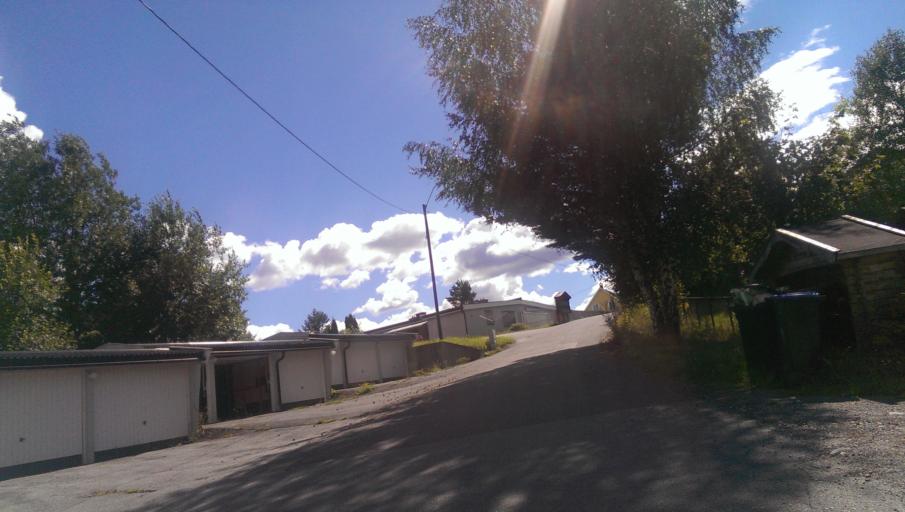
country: NO
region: Buskerud
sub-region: Kongsberg
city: Kongsberg
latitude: 59.6575
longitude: 9.6554
